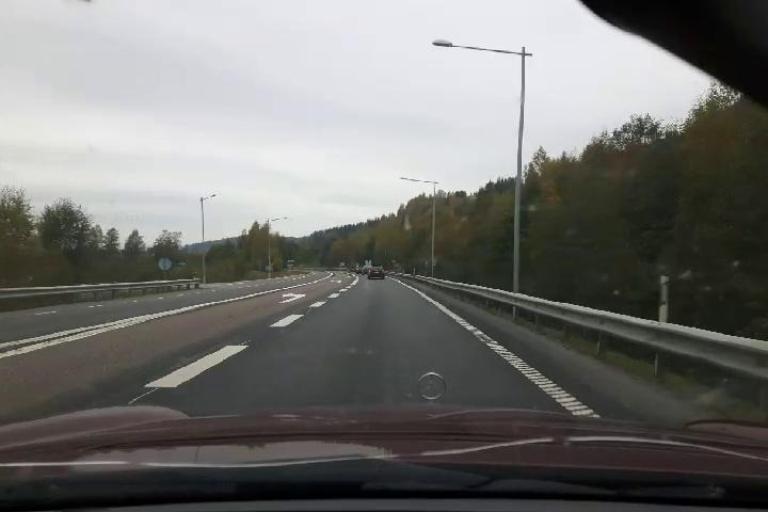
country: SE
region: Vaesternorrland
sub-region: OErnskoeldsviks Kommun
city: Ornskoldsvik
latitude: 63.2978
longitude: 18.6553
